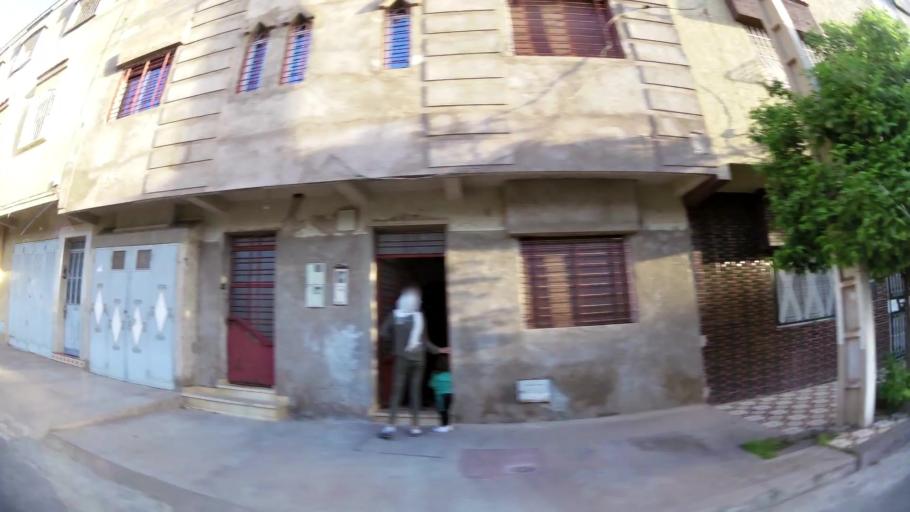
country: MA
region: Oriental
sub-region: Oujda-Angad
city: Oujda
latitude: 34.6792
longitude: -1.8902
